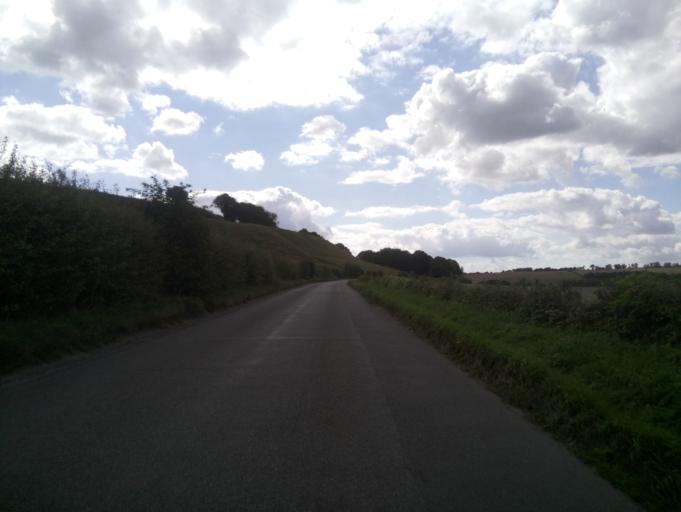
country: GB
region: England
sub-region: Wiltshire
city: Salisbury
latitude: 51.0962
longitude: -1.8040
